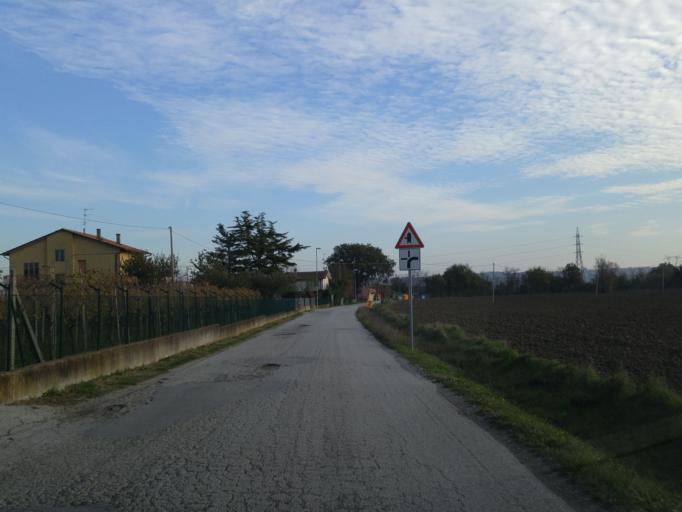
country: IT
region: The Marches
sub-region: Provincia di Pesaro e Urbino
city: Cuccurano
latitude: 43.7910
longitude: 12.9581
